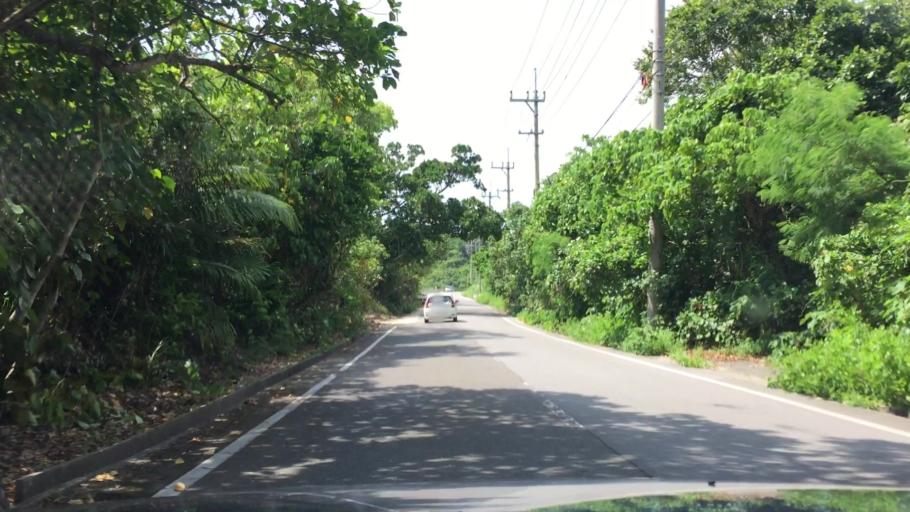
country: JP
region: Okinawa
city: Ishigaki
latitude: 24.4653
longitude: 124.2266
